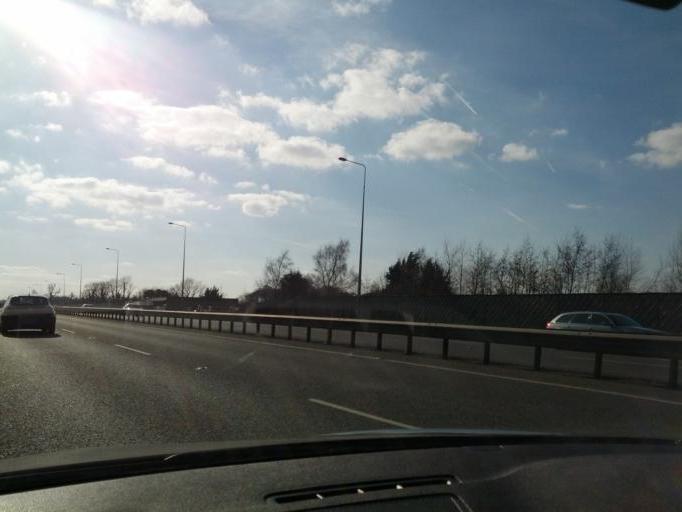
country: IE
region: Leinster
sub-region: Kildare
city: Kill
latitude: 53.2448
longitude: -6.6041
